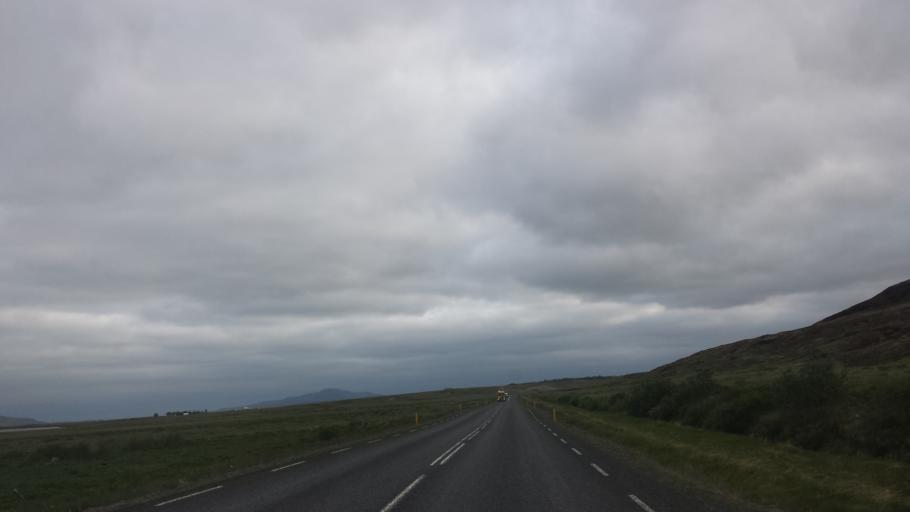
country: IS
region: South
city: Selfoss
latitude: 64.1357
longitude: -20.5762
